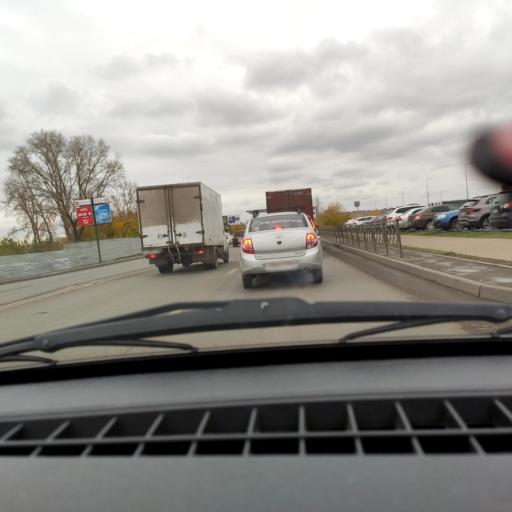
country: RU
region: Bashkortostan
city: Ufa
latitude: 54.7953
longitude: 56.0770
